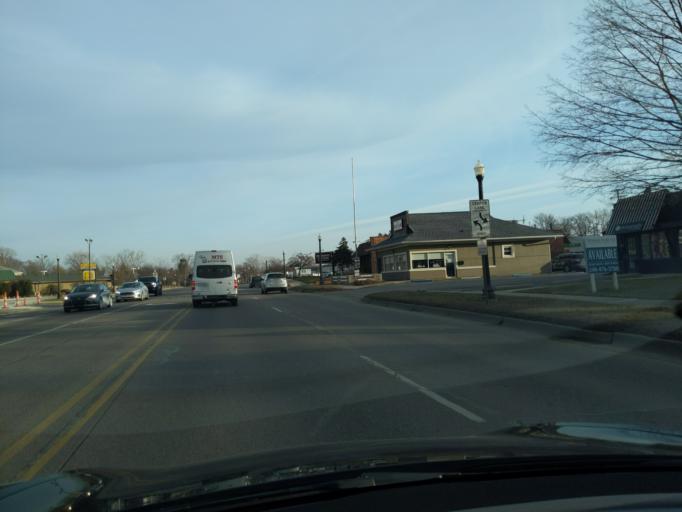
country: US
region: Michigan
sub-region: Livingston County
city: Howell
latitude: 42.6027
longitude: -83.9175
